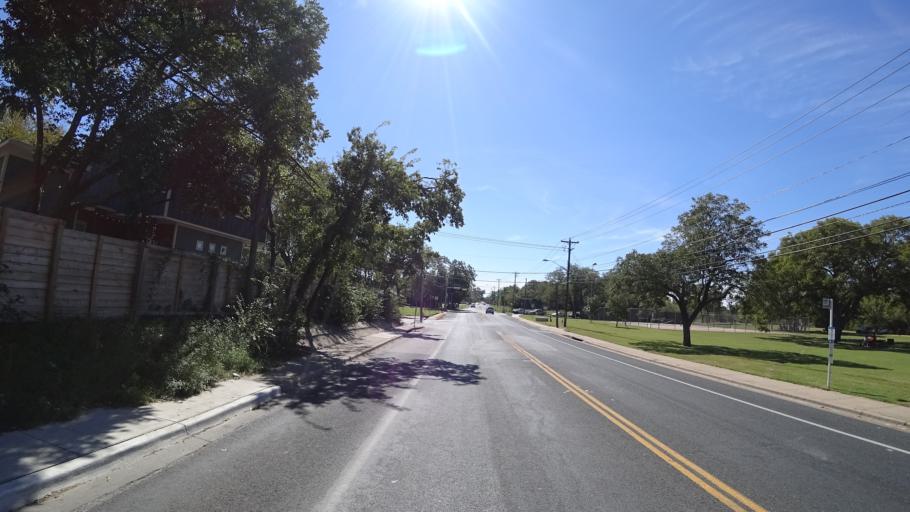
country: US
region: Texas
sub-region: Travis County
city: Austin
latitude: 30.2743
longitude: -97.6899
